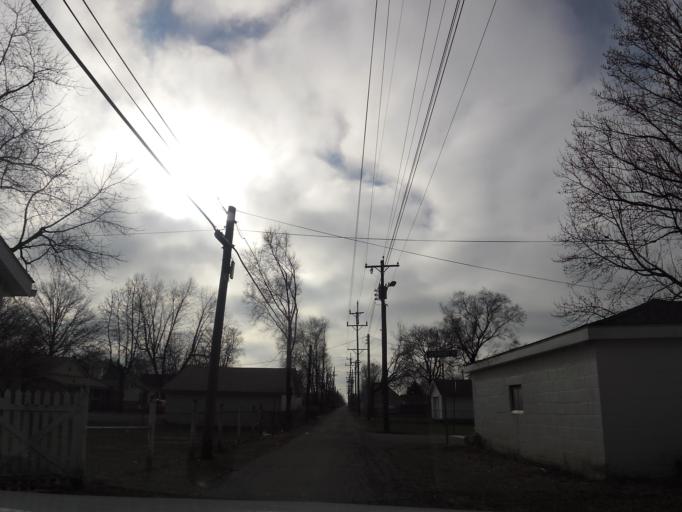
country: US
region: Indiana
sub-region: Bartholomew County
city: Columbus
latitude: 39.1958
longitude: -85.9039
